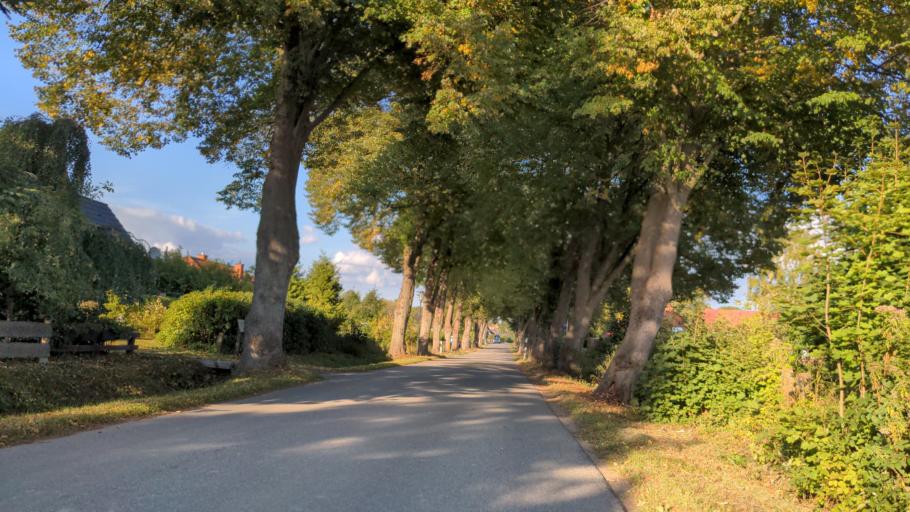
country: DE
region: Schleswig-Holstein
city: Ahrensbok
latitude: 53.9771
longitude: 10.6267
